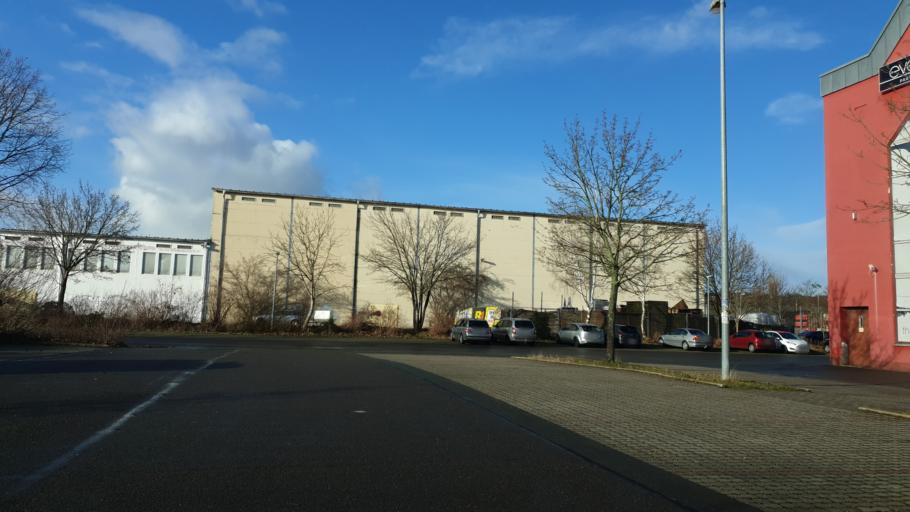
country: DE
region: Thuringia
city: Gera
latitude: 50.8985
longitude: 12.0705
